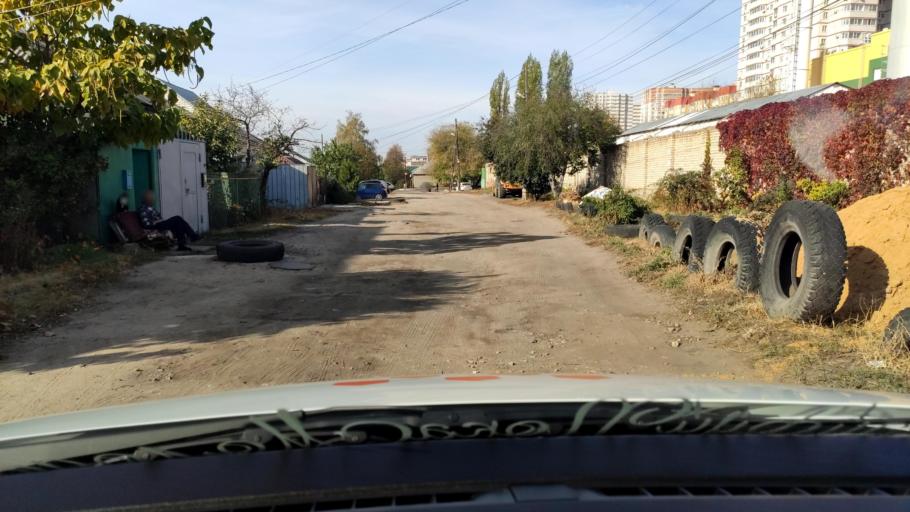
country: RU
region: Voronezj
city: Voronezh
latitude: 51.6699
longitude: 39.1548
